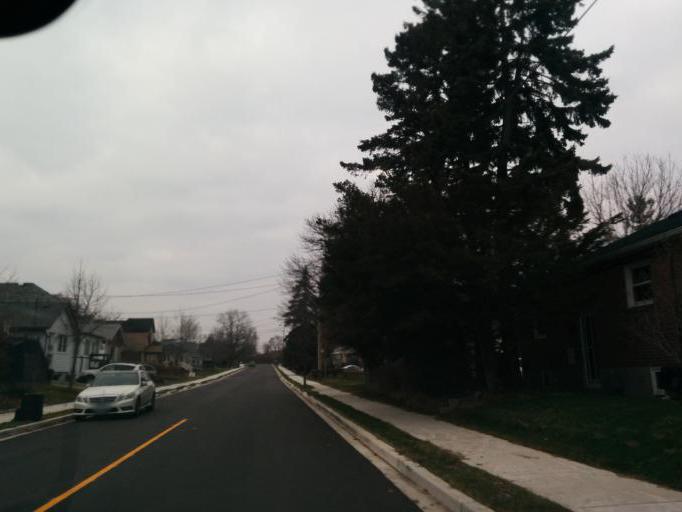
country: CA
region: Ontario
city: Etobicoke
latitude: 43.5907
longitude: -79.5395
